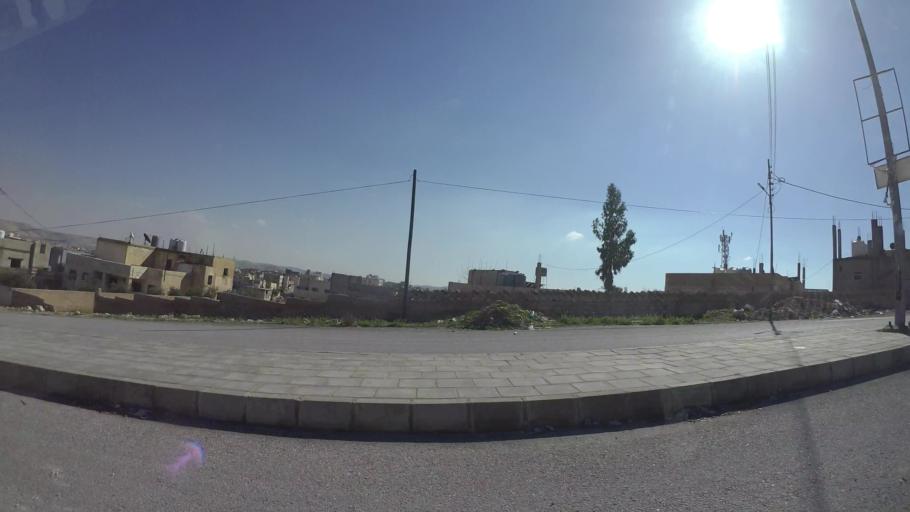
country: JO
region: Zarqa
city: Russeifa
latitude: 32.0425
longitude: 36.0414
